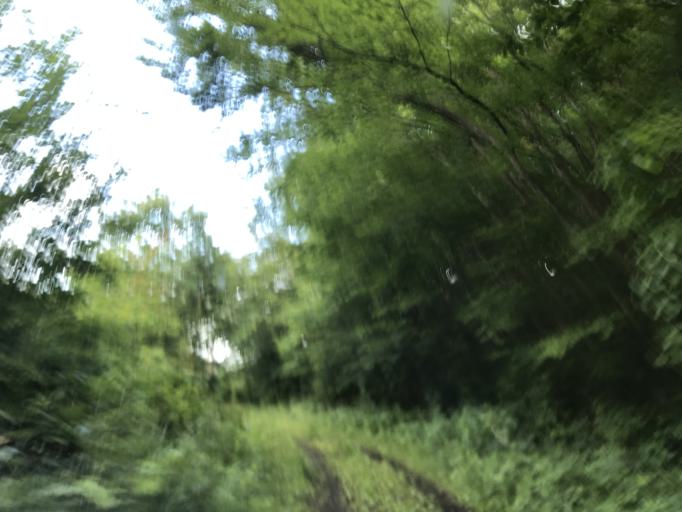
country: JP
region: Iwate
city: Ichinoseki
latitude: 38.9075
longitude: 140.9495
